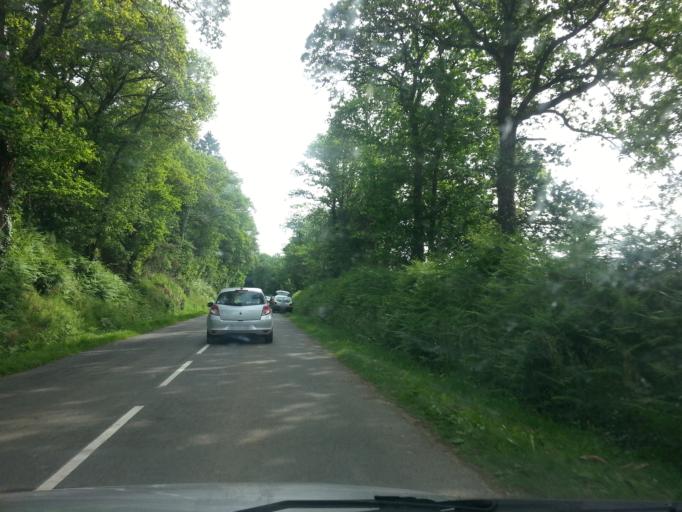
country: FR
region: Brittany
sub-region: Departement du Morbihan
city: Le Faouet
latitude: 47.9888
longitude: -3.4902
